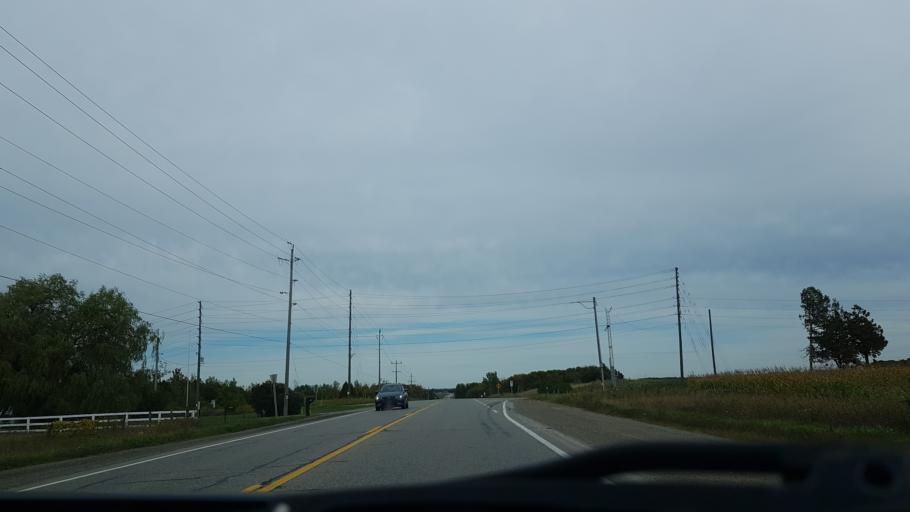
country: CA
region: Ontario
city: Orangeville
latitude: 43.8100
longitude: -80.0508
